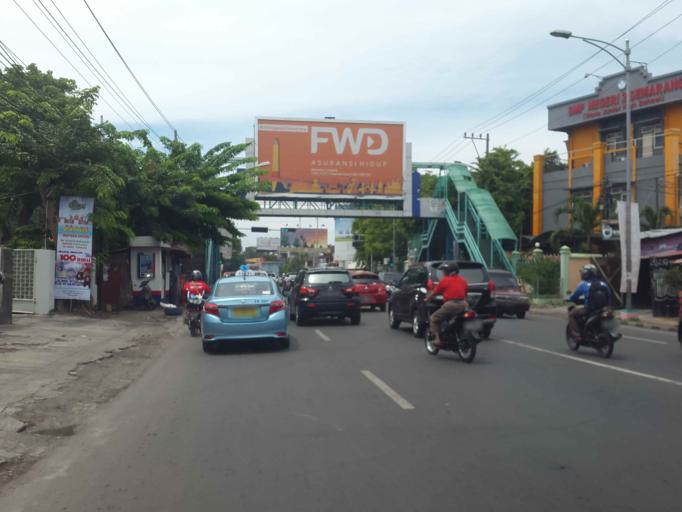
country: ID
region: Central Java
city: Semarang
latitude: -6.9954
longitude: 110.4349
